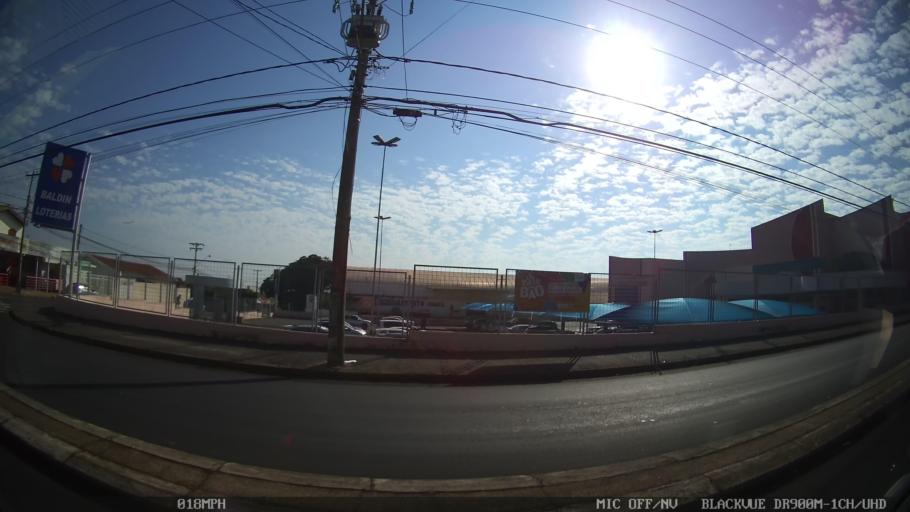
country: BR
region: Sao Paulo
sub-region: Americana
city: Americana
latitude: -22.7304
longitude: -47.3426
